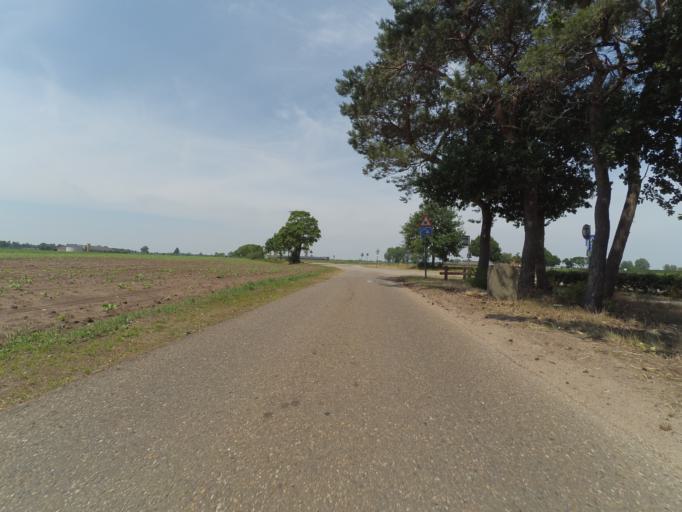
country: BE
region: Flanders
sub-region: Provincie Antwerpen
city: Wuustwezel
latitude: 51.4182
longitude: 4.5894
